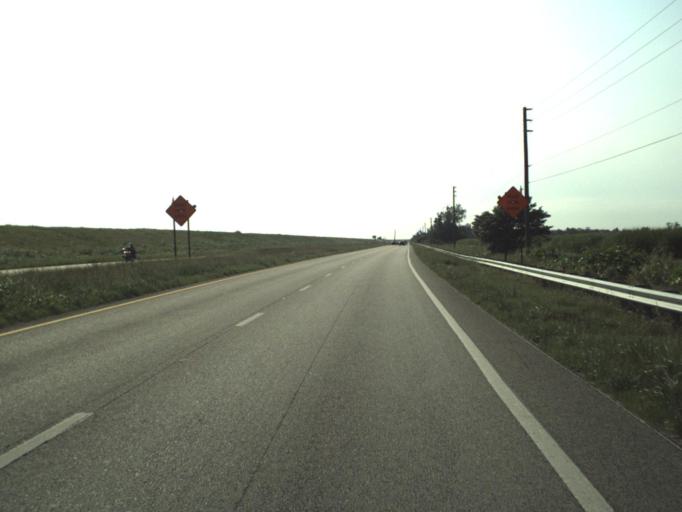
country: US
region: Florida
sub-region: Hendry County
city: Clewiston
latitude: 26.7382
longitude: -80.8741
